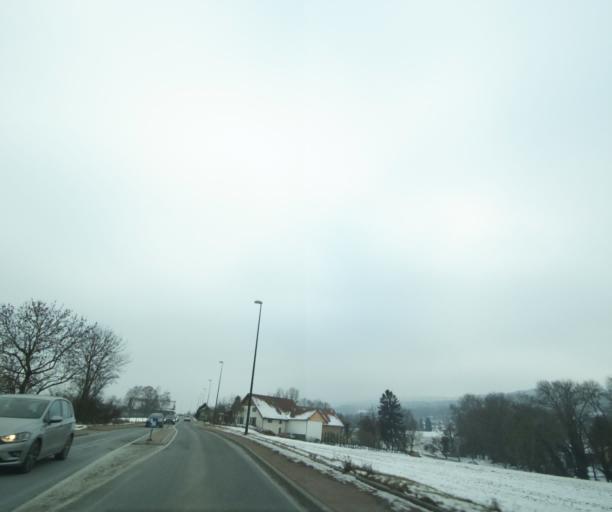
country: FR
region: Rhone-Alpes
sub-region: Departement de la Haute-Savoie
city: Pers-Jussy
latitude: 46.1151
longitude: 6.2726
